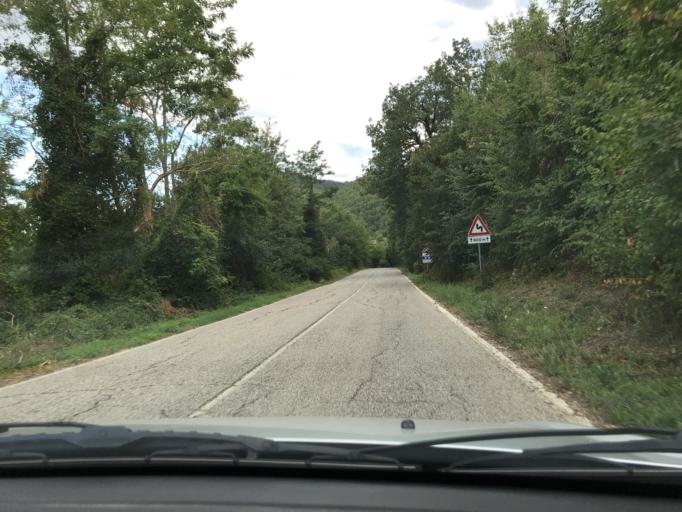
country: IT
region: Umbria
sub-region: Provincia di Terni
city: Montecchio
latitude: 42.6648
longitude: 12.3360
